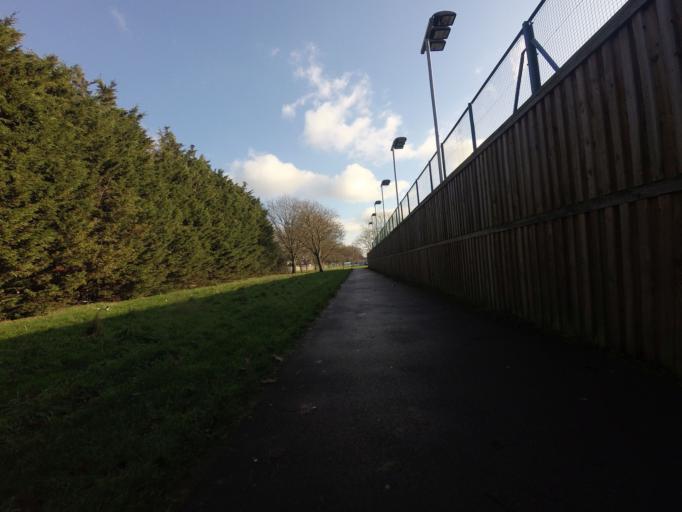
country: GB
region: England
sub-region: Greater London
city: Feltham
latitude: 51.4419
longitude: -0.3933
